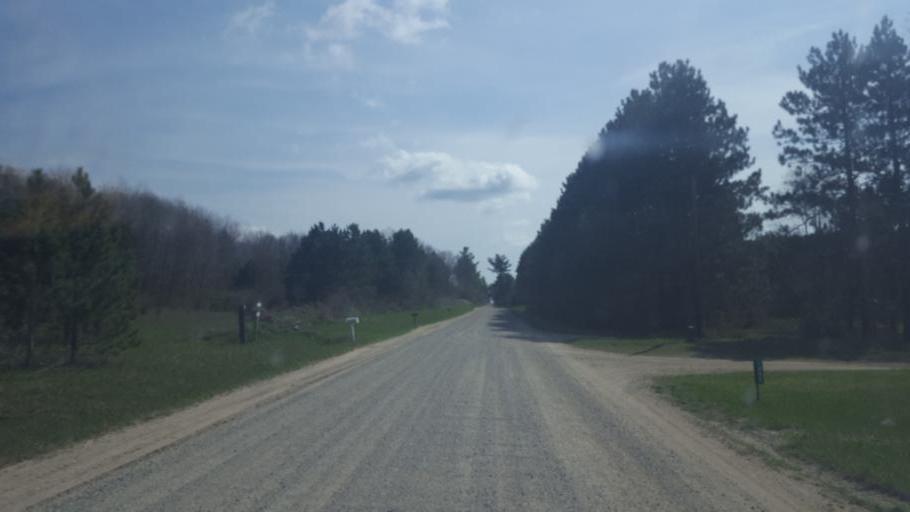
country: US
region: Michigan
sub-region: Montcalm County
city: Edmore
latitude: 43.4592
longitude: -84.9364
